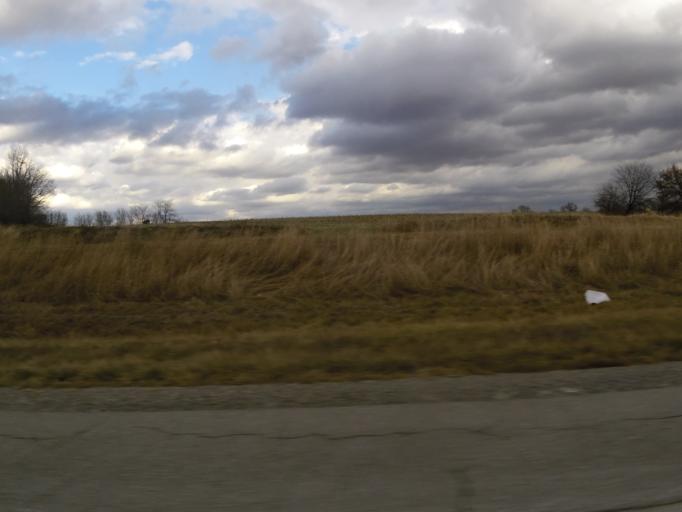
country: US
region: Missouri
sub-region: Ralls County
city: New London
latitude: 39.5081
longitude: -91.3269
